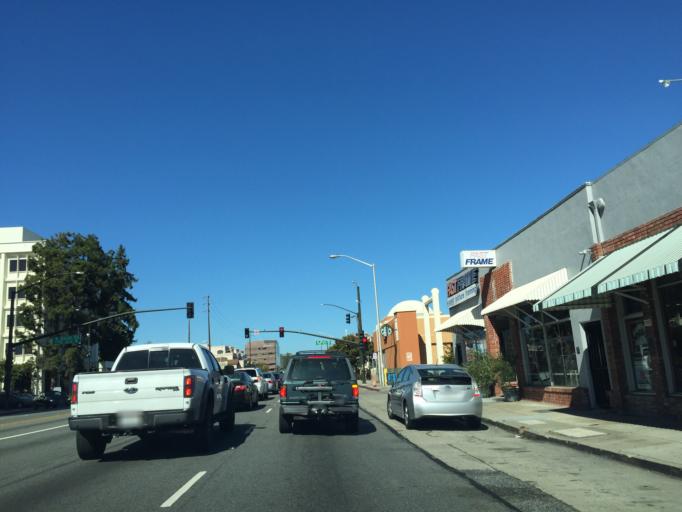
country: US
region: California
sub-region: San Mateo County
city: San Mateo
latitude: 37.5518
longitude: -122.3135
